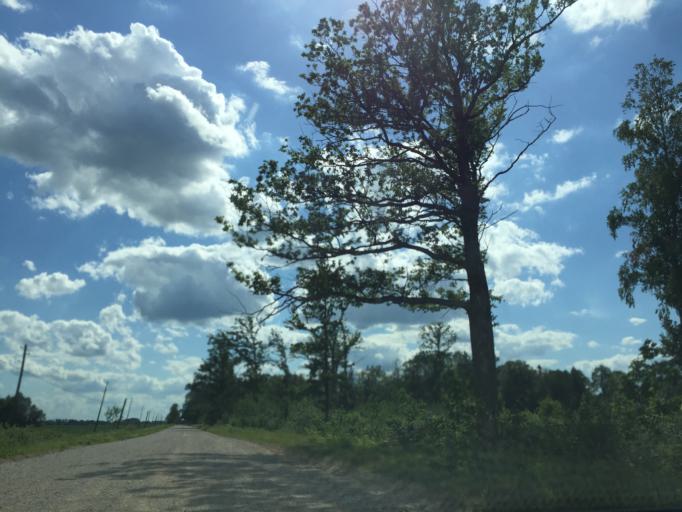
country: LV
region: Engure
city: Smarde
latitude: 56.8650
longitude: 23.3236
